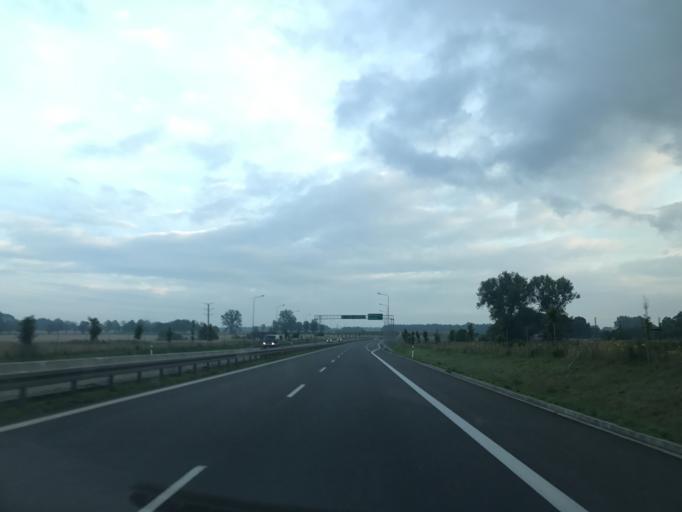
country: PL
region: West Pomeranian Voivodeship
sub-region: Powiat goleniowski
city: Nowogard
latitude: 53.6615
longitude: 15.0772
